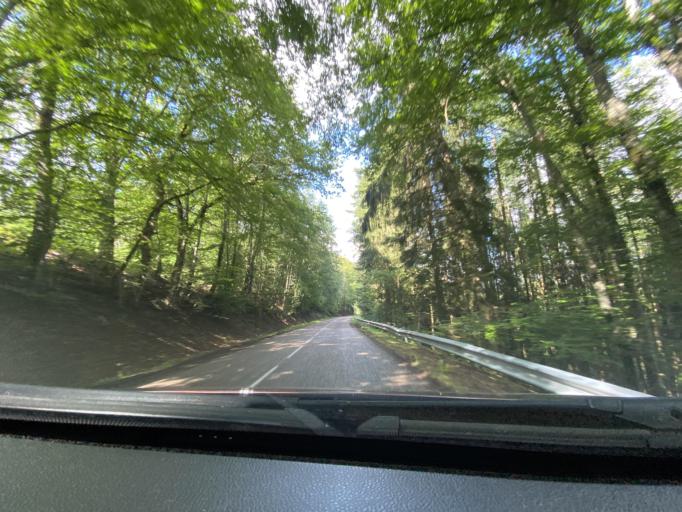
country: FR
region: Bourgogne
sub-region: Departement de la Cote-d'Or
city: Saulieu
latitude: 47.2708
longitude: 4.1262
